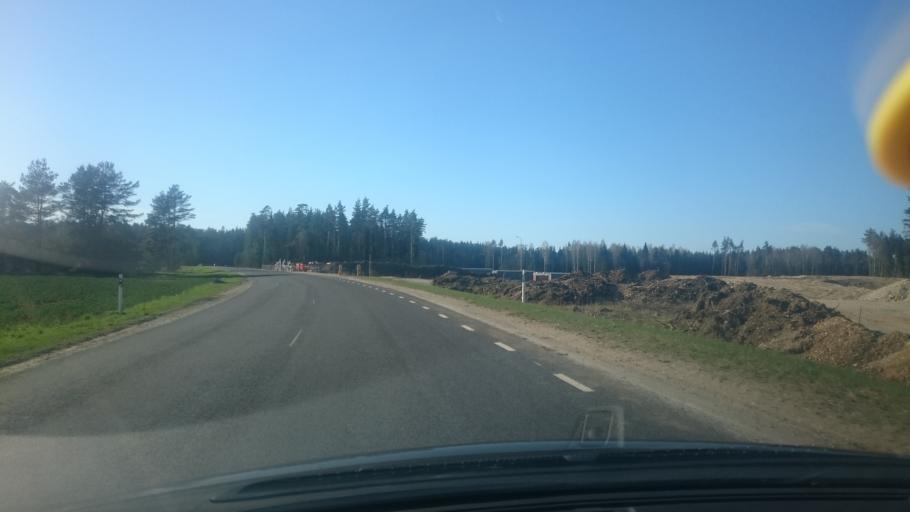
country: EE
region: Harju
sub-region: Raasiku vald
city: Raasiku
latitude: 59.1566
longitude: 25.1903
